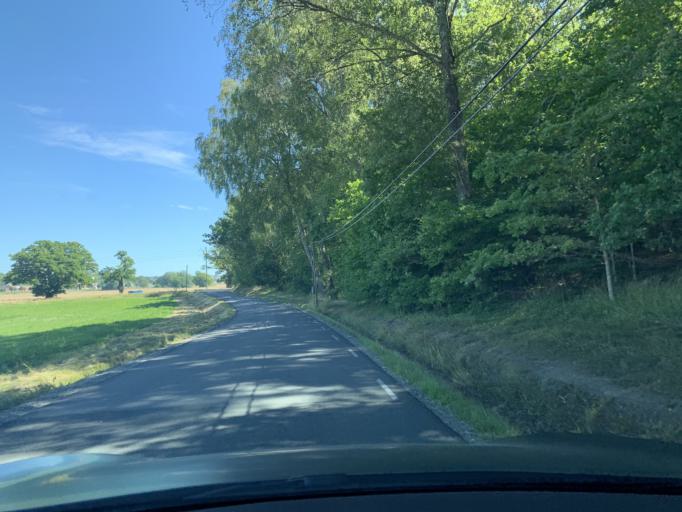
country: SE
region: Stockholm
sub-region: Botkyrka Kommun
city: Eriksberg
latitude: 59.2509
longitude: 17.7761
